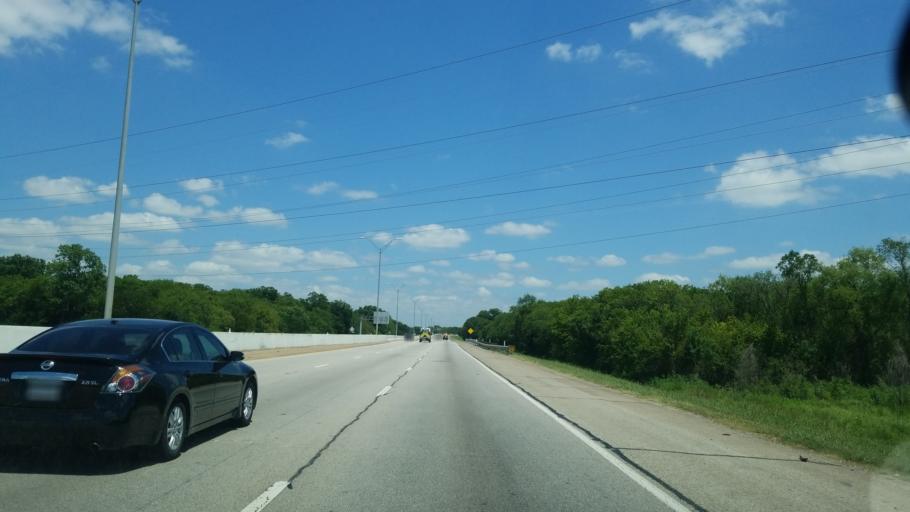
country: US
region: Texas
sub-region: Dallas County
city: Dallas
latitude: 32.7464
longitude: -96.7369
